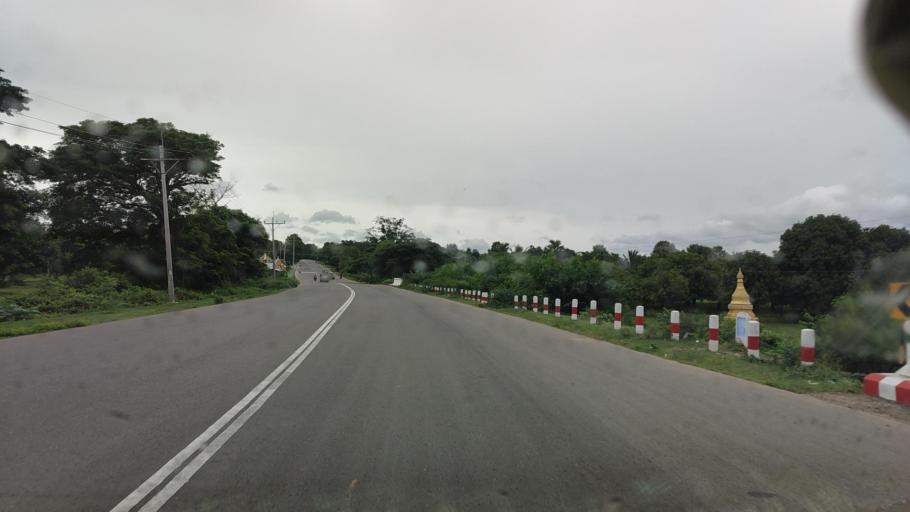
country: MM
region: Mandalay
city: Meiktila
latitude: 20.8135
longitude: 95.9077
